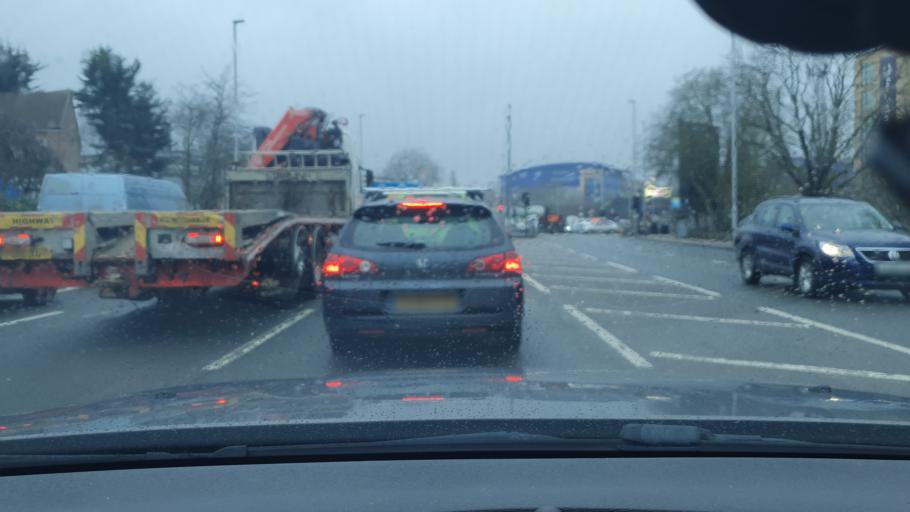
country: GB
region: England
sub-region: Greater London
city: Wood Green
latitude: 51.6118
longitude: -0.1346
